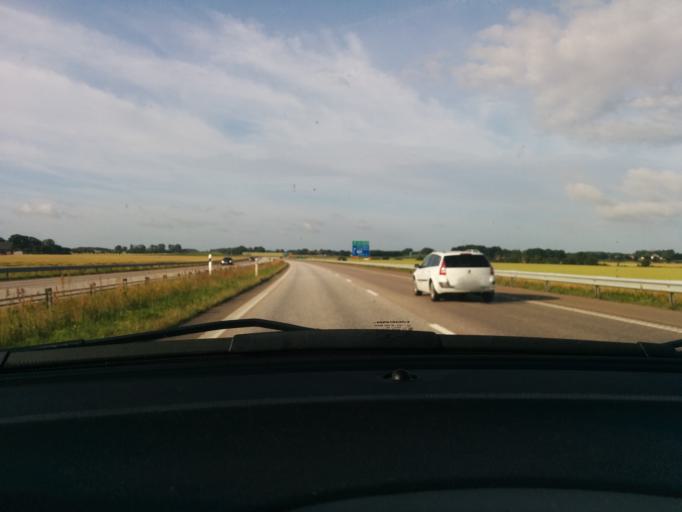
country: SE
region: Skane
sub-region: Angelholms Kommun
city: Strovelstorp
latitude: 56.1168
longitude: 12.8146
